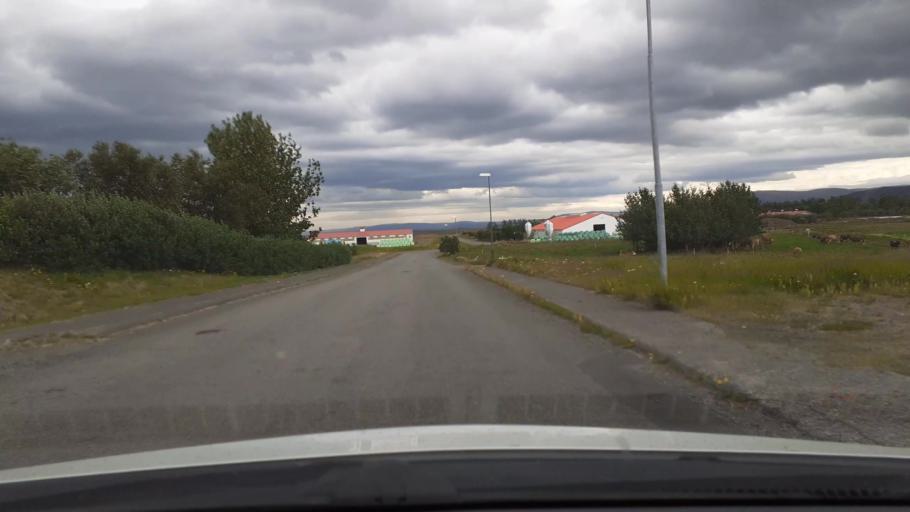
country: IS
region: West
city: Borgarnes
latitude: 64.5668
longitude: -21.7612
